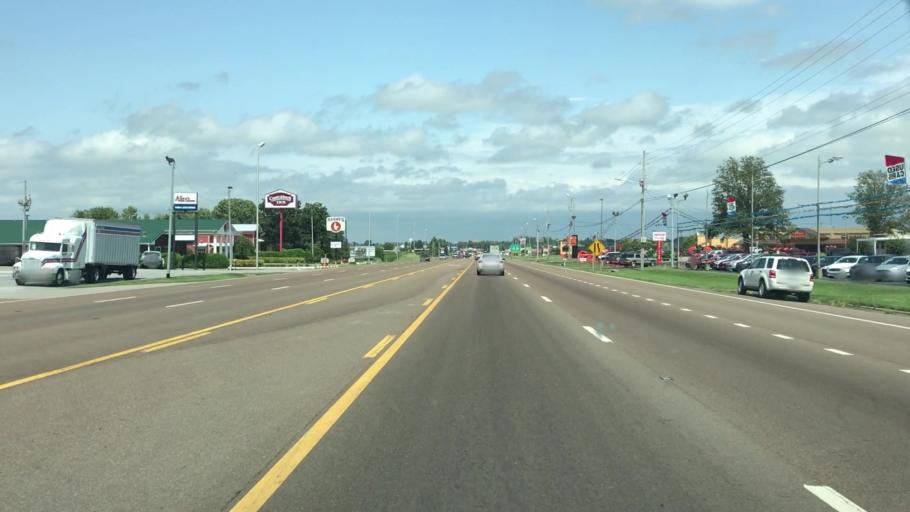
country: US
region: Tennessee
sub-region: Obion County
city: Union City
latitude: 36.4076
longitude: -89.0832
